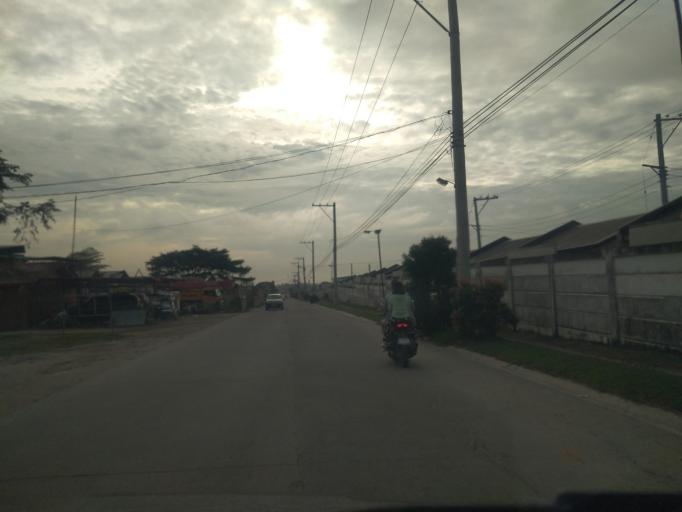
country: PH
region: Central Luzon
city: Santol
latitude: 15.1673
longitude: 120.5371
